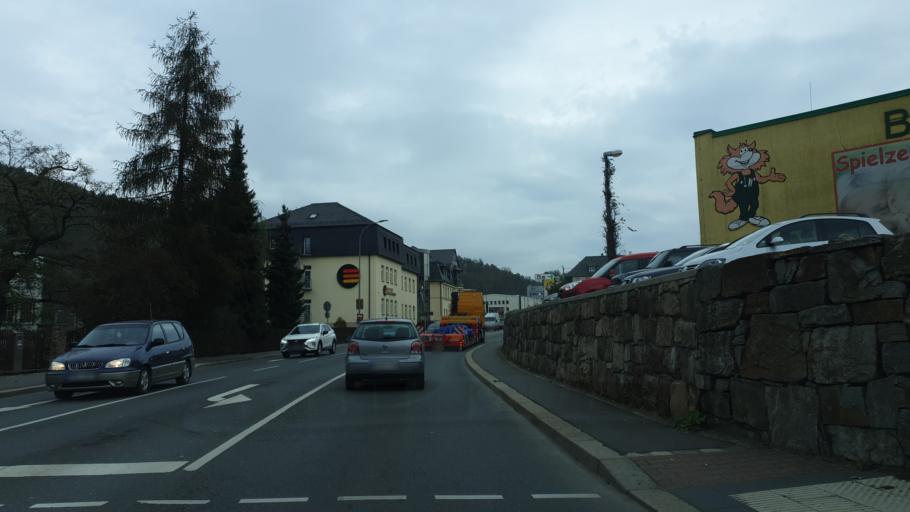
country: DE
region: Saxony
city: Schwarzenberg
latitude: 50.5471
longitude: 12.7856
